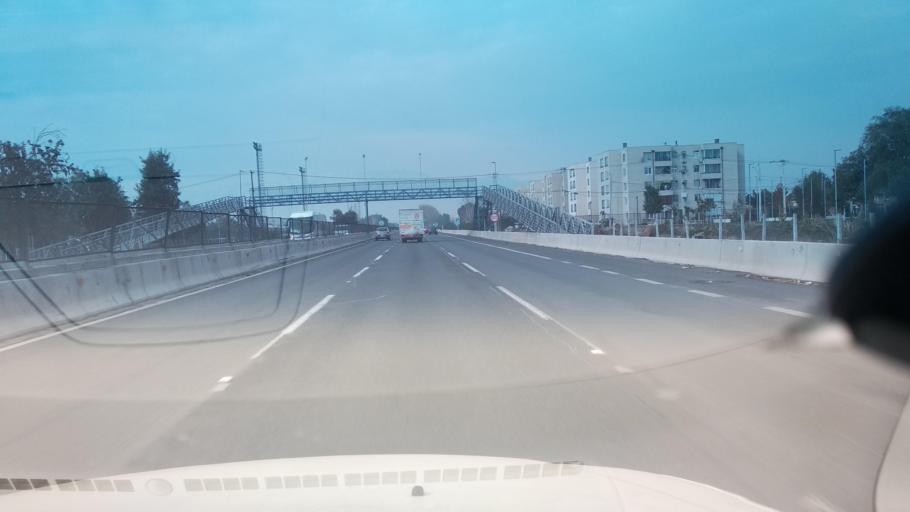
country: CL
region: Santiago Metropolitan
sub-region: Provincia de Santiago
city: Lo Prado
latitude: -33.4512
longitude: -70.7511
